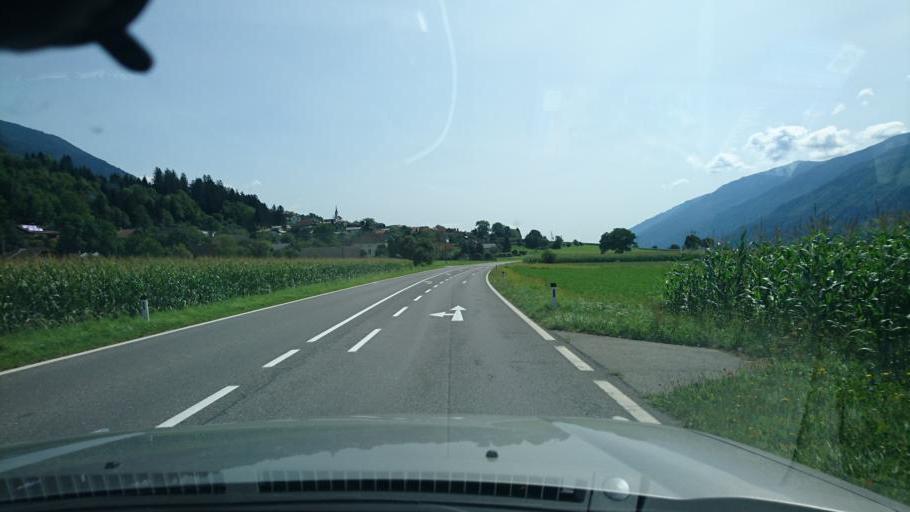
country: AT
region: Carinthia
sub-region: Politischer Bezirk Spittal an der Drau
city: Muhldorf
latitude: 46.8483
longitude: 13.3645
